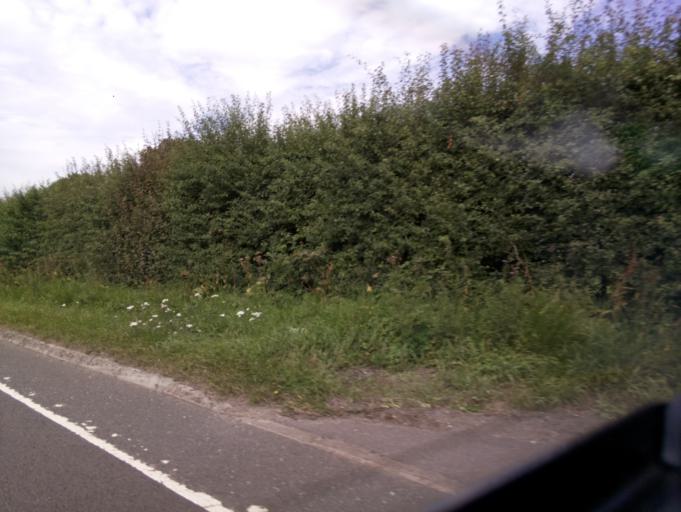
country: GB
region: England
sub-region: Somerset
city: Yeovil
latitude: 50.8705
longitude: -2.5963
